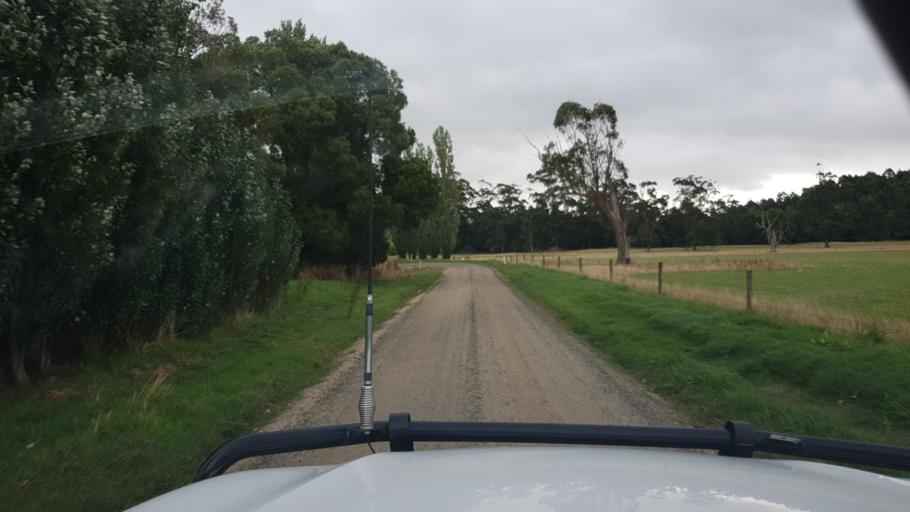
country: AU
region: Victoria
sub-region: Baw Baw
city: Warragul
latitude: -38.2549
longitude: 145.9359
